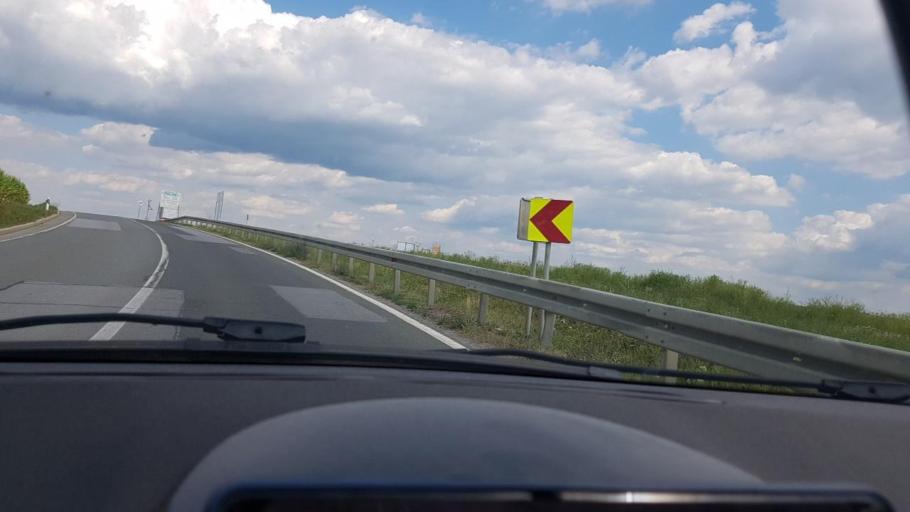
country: HR
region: Bjelovarsko-Bilogorska
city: Zdralovi
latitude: 45.8722
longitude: 16.8885
